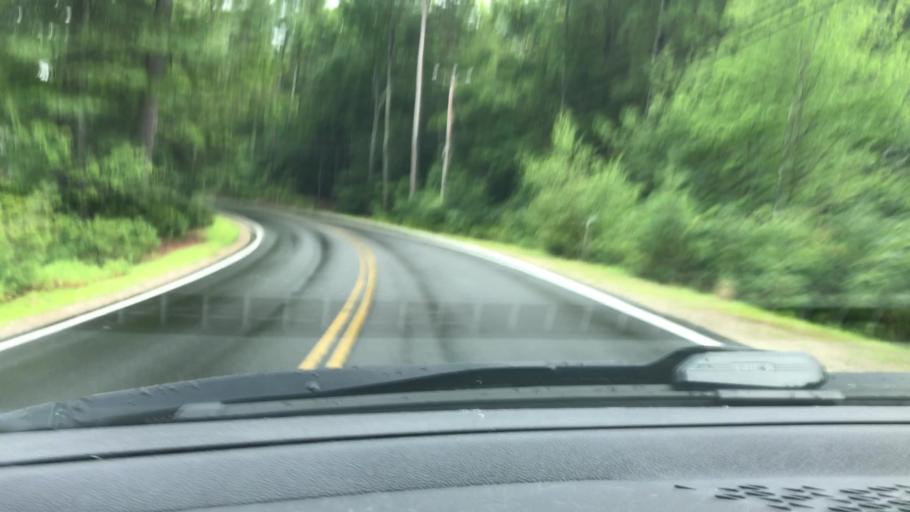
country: US
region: New Hampshire
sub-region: Rockingham County
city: Candia
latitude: 43.1559
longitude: -71.2376
